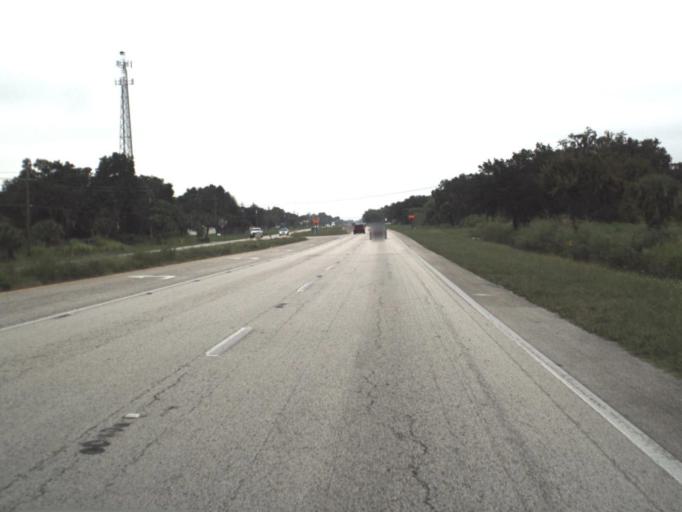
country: US
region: Florida
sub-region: Manatee County
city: Memphis
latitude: 27.6030
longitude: -82.5394
